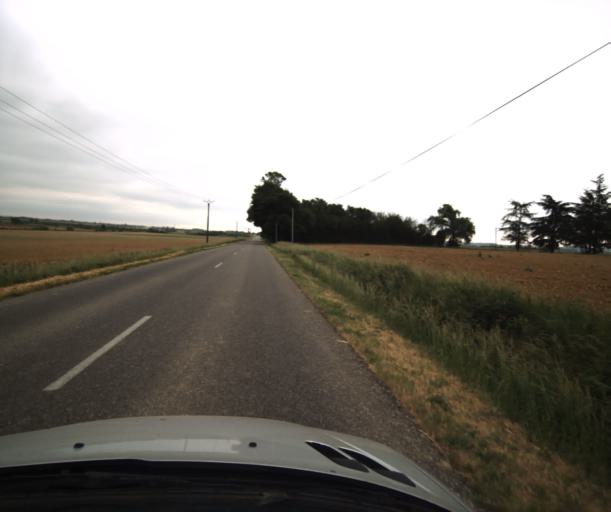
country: FR
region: Midi-Pyrenees
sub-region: Departement du Tarn-et-Garonne
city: Saint-Nicolas-de-la-Grave
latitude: 44.0348
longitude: 1.0125
